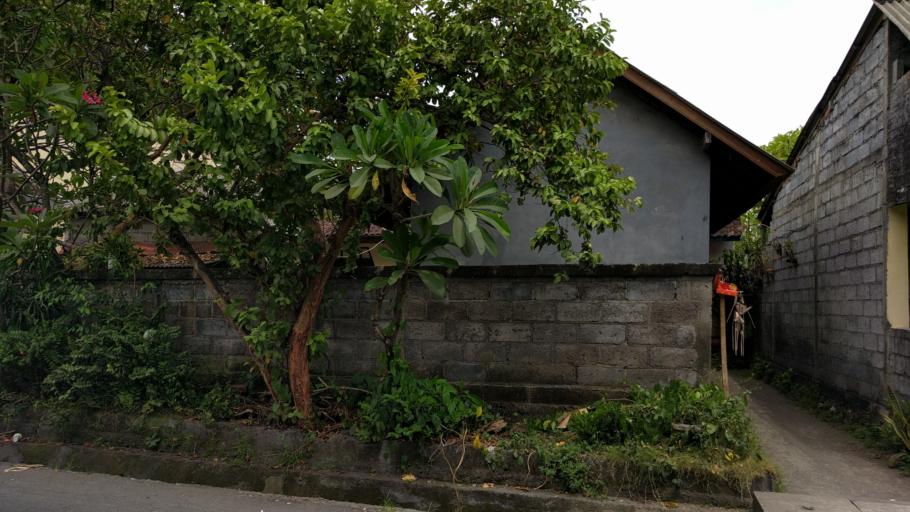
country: ID
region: Bali
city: Banjar Gunungpande
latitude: -8.6428
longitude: 115.1547
